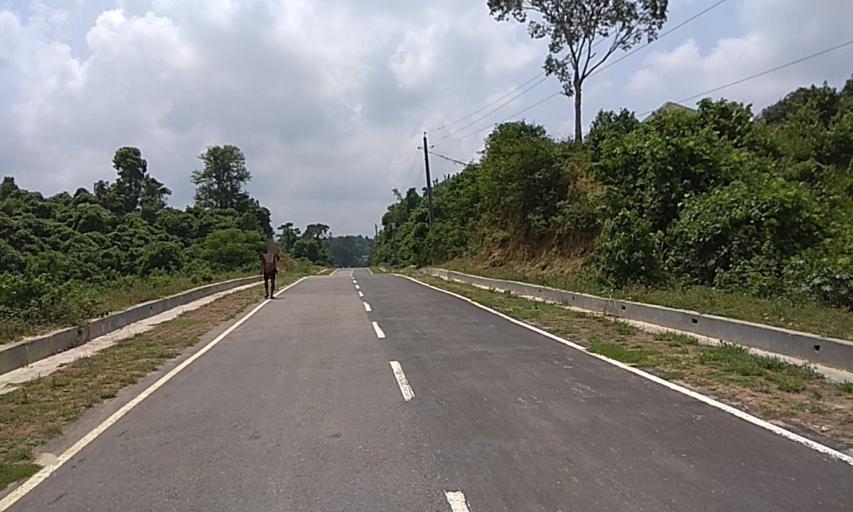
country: BD
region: Chittagong
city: Manikchari
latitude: 22.9373
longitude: 91.9058
